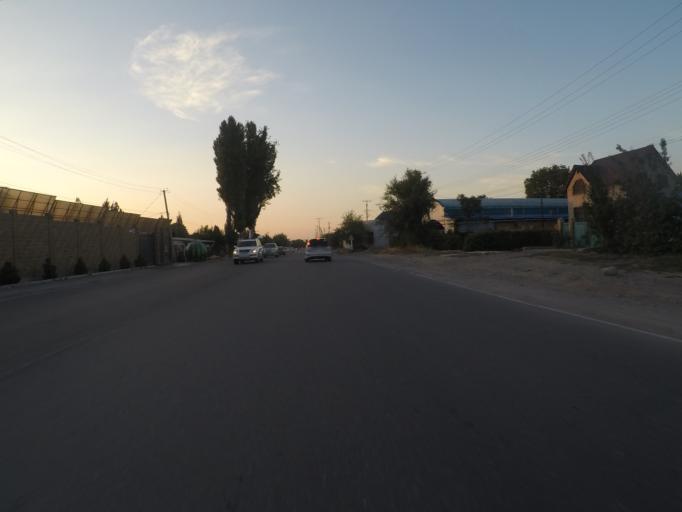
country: KG
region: Chuy
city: Lebedinovka
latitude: 42.8092
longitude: 74.6466
